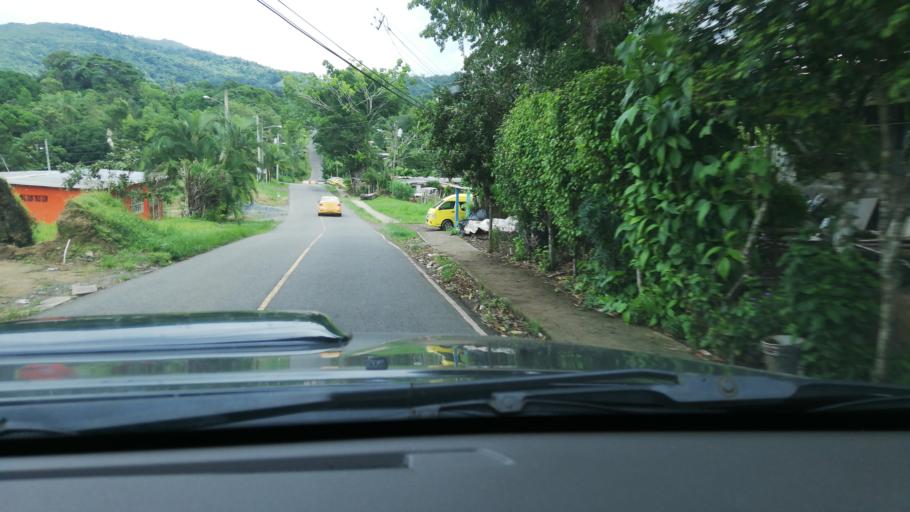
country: PA
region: Panama
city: San Miguelito
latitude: 9.1037
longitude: -79.4466
